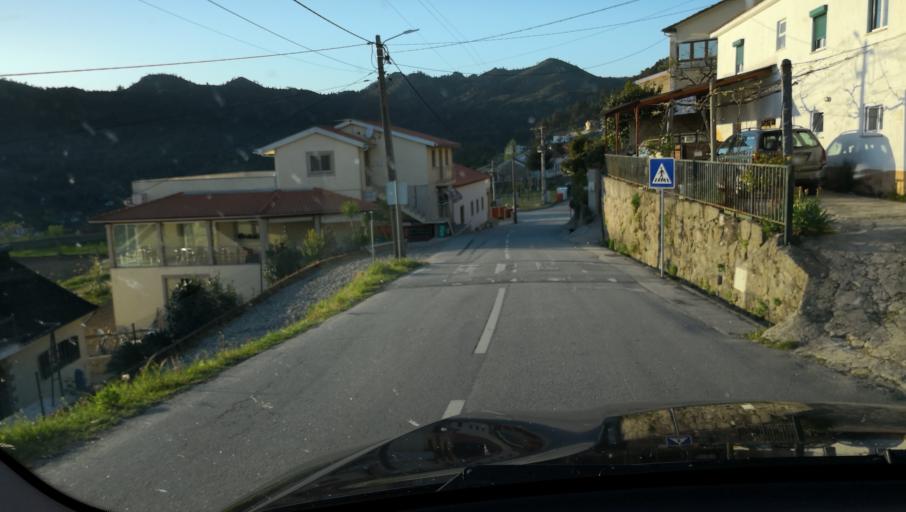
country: PT
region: Vila Real
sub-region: Mondim de Basto
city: Mondim de Basto
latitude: 41.4133
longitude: -7.8787
